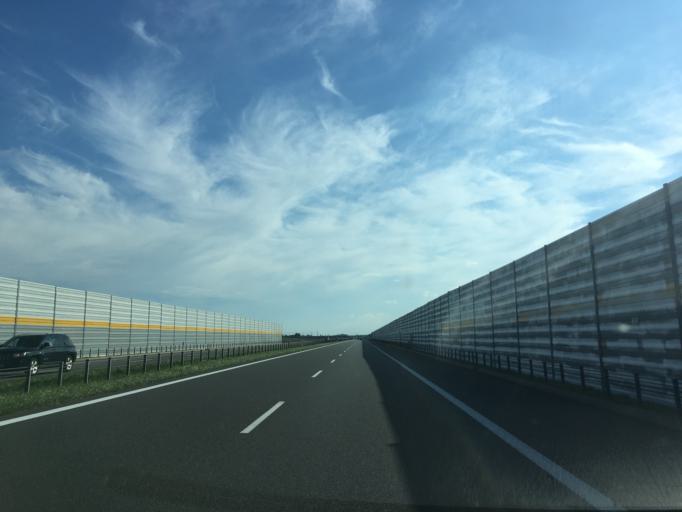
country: PL
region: Kujawsko-Pomorskie
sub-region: Powiat chelminski
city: Lisewo
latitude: 53.3071
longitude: 18.7062
